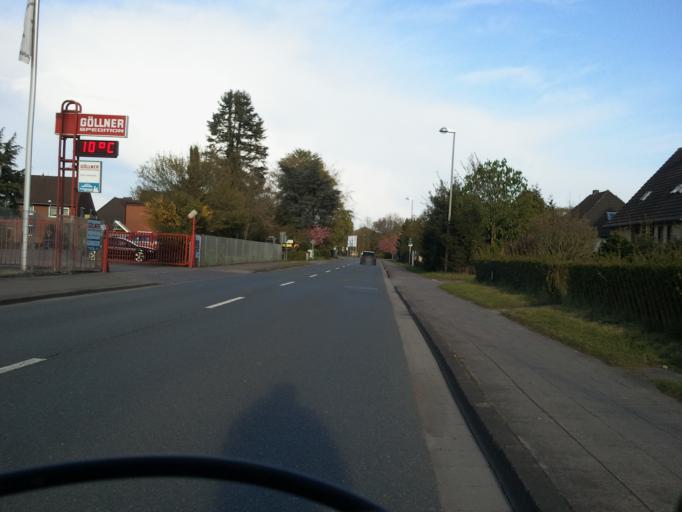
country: DE
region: Lower Saxony
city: Nienburg
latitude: 52.6412
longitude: 9.2263
